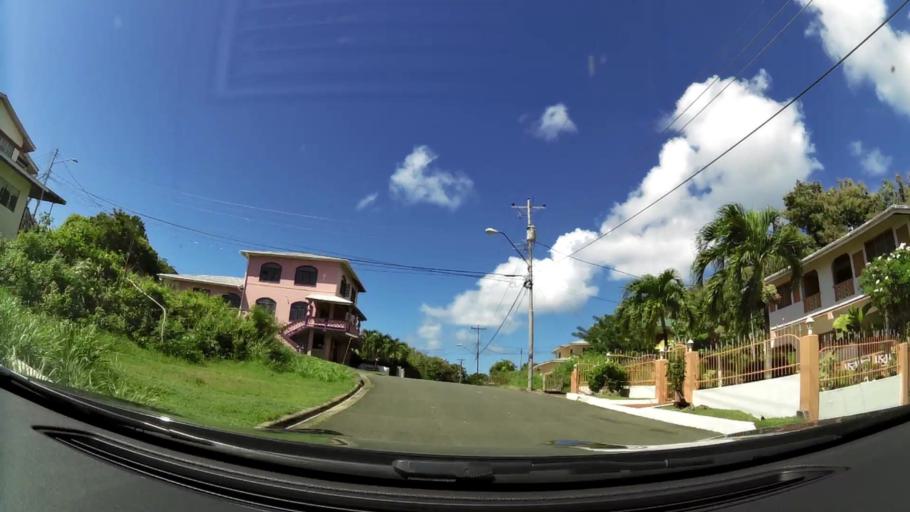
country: TT
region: Tobago
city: Scarborough
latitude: 11.1747
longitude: -60.7885
